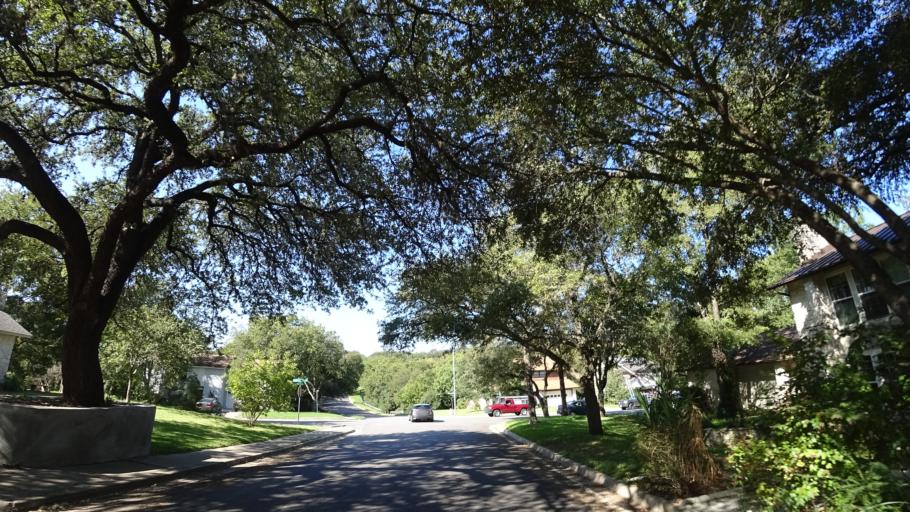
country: US
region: Texas
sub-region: Travis County
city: Rollingwood
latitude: 30.2735
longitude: -97.8051
